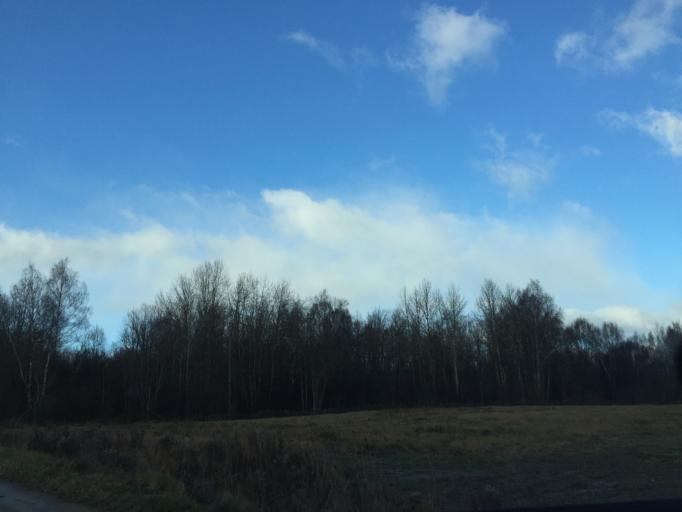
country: LV
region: Valmieras Rajons
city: Valmiera
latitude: 57.5374
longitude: 25.3883
